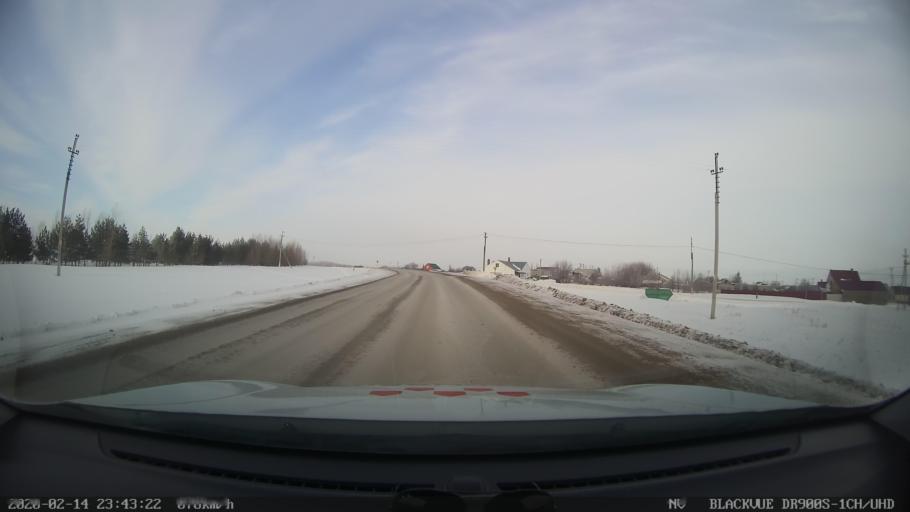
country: RU
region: Tatarstan
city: Kuybyshevskiy Zaton
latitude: 55.2009
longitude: 49.2497
